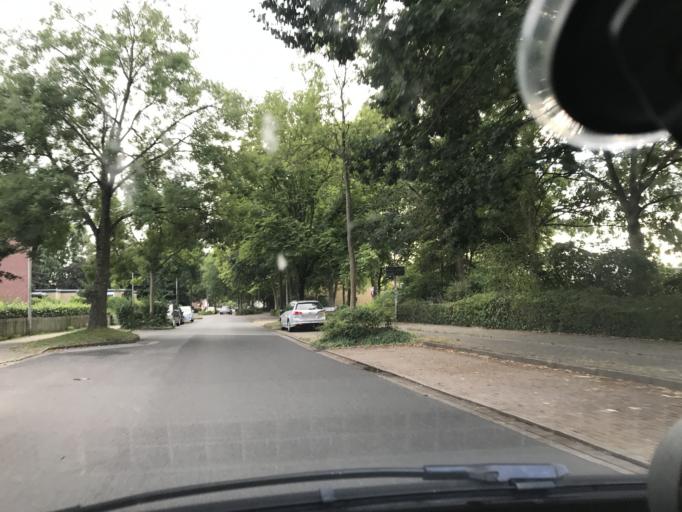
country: DE
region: Lower Saxony
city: Buxtehude
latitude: 53.4776
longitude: 9.6955
